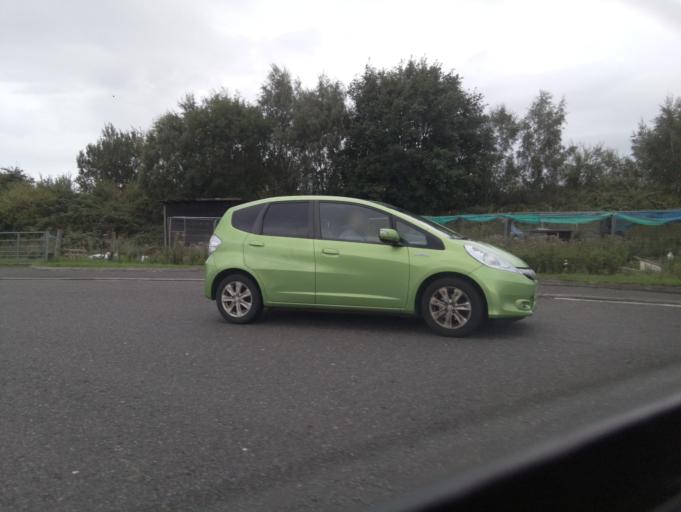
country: GB
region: Scotland
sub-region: Clackmannanshire
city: Clackmannan
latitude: 56.1141
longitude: -3.7580
